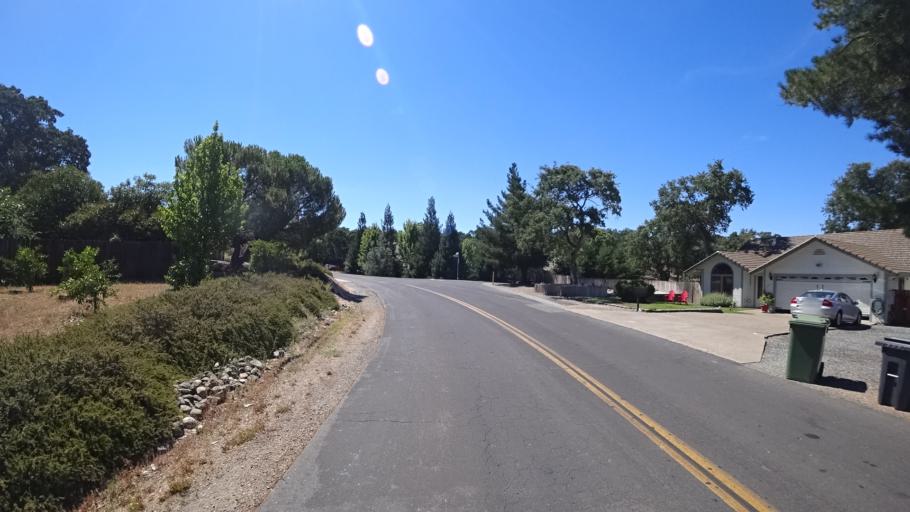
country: US
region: California
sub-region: Calaveras County
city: Valley Springs
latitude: 38.1611
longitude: -120.8347
